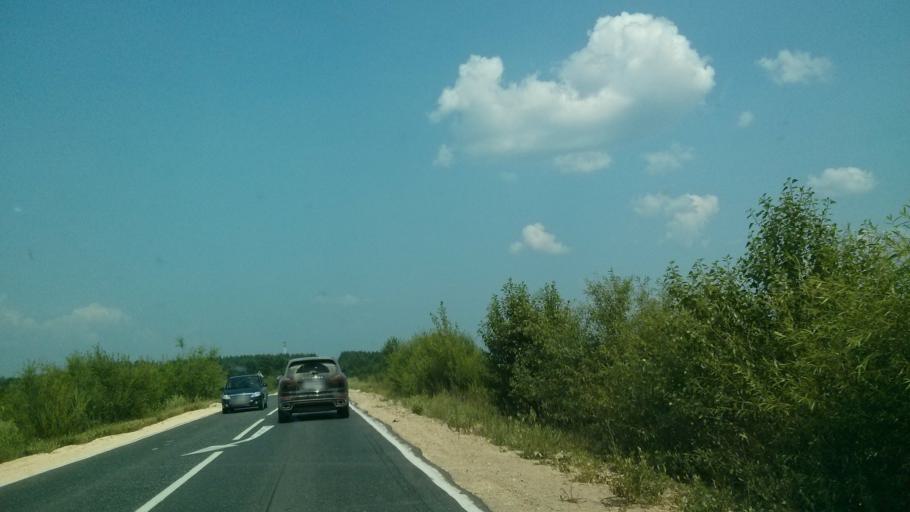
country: RU
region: Nizjnij Novgorod
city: Navashino
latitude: 55.5940
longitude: 42.1548
